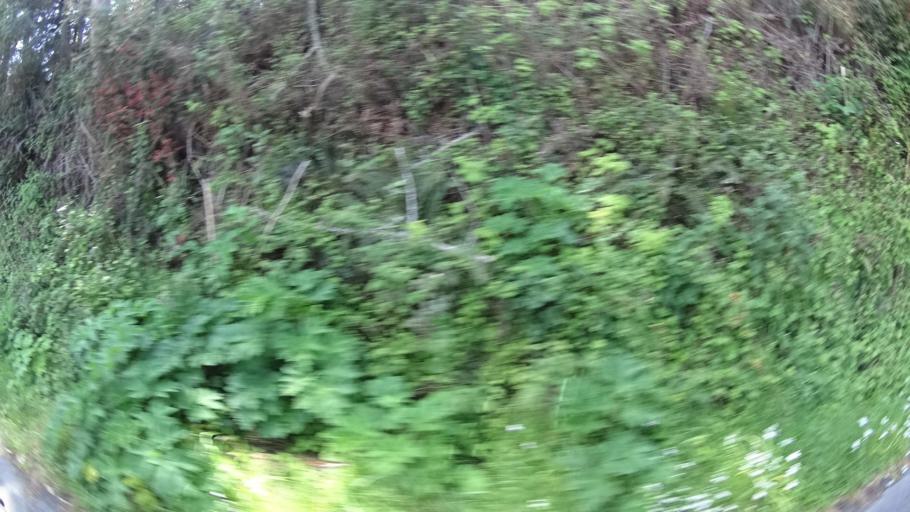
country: US
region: California
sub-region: Humboldt County
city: Humboldt Hill
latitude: 40.6732
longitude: -124.2175
